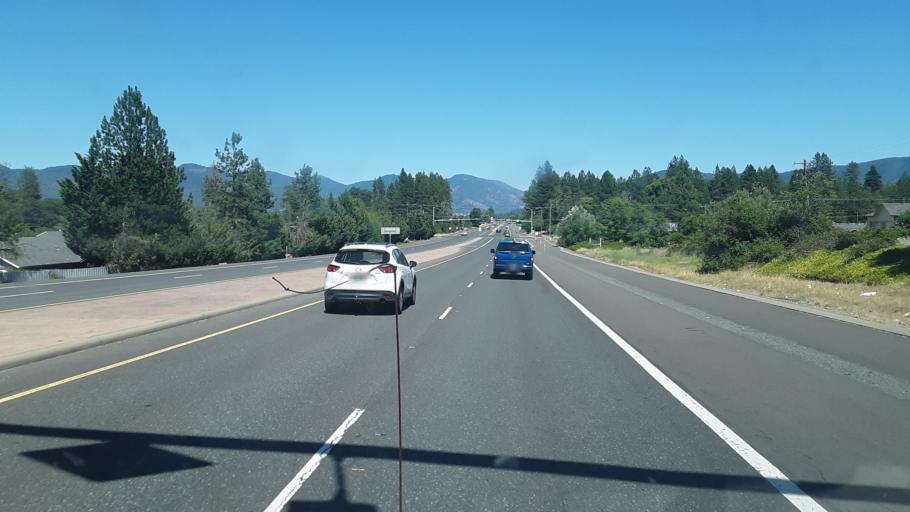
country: US
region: Oregon
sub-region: Josephine County
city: Redwood
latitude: 42.4152
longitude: -123.3900
